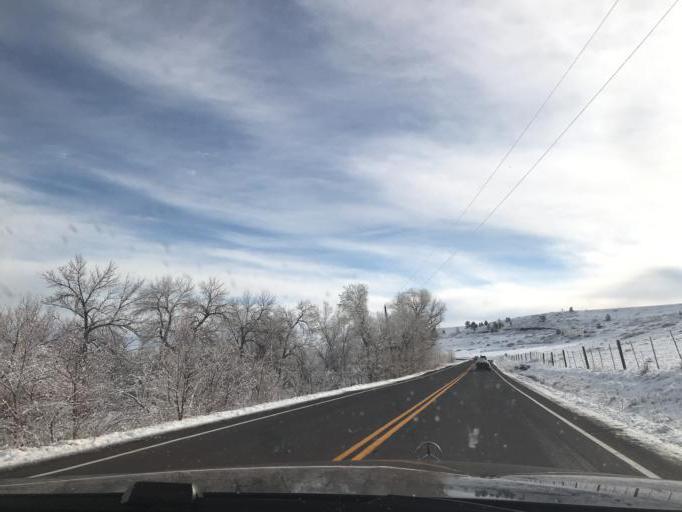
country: US
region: Colorado
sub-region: Boulder County
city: Superior
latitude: 39.9609
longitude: -105.2190
